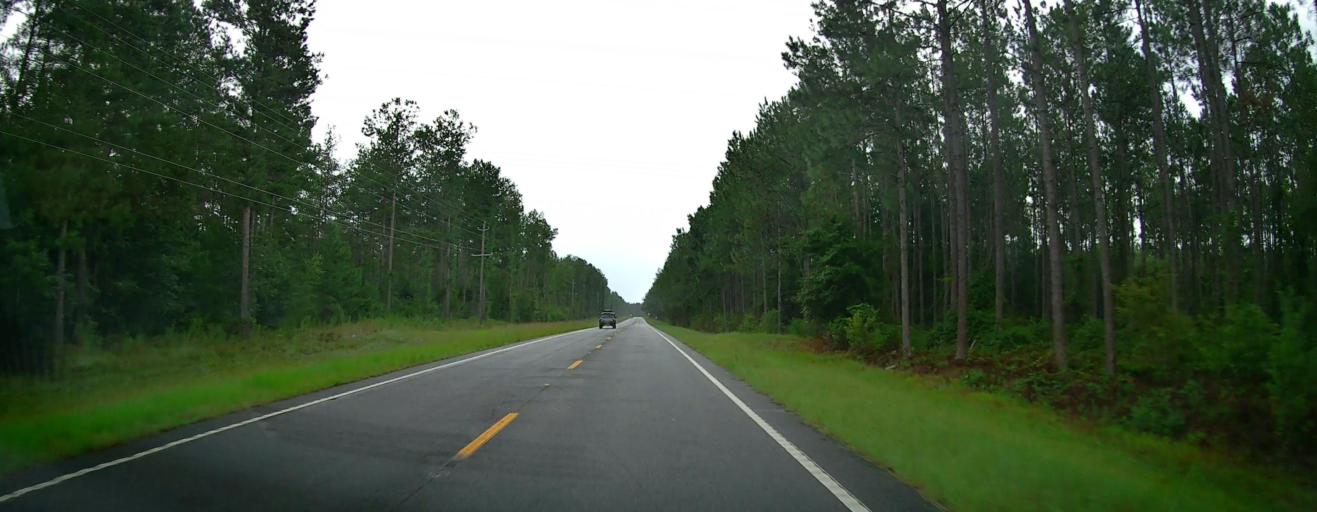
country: US
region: Georgia
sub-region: Ware County
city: Deenwood
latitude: 31.2774
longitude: -82.5357
